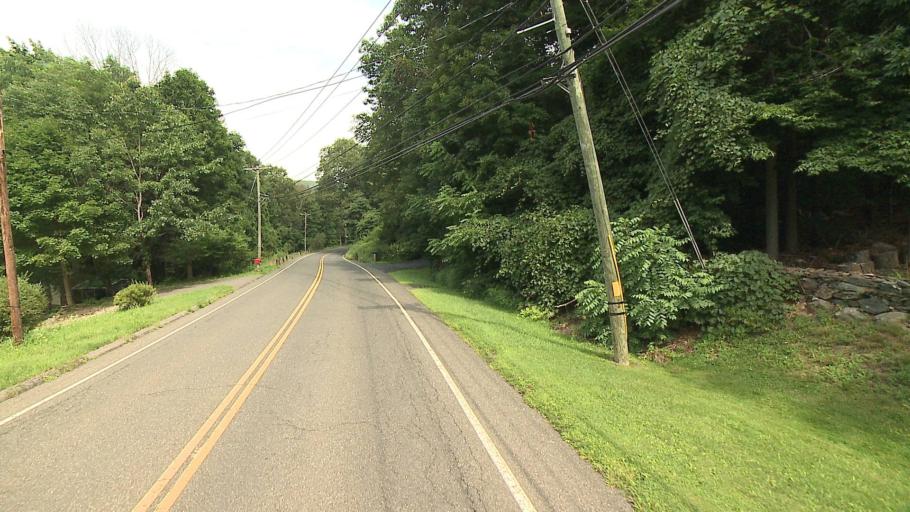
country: US
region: Connecticut
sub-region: Fairfield County
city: Sherman
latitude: 41.5408
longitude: -73.4791
